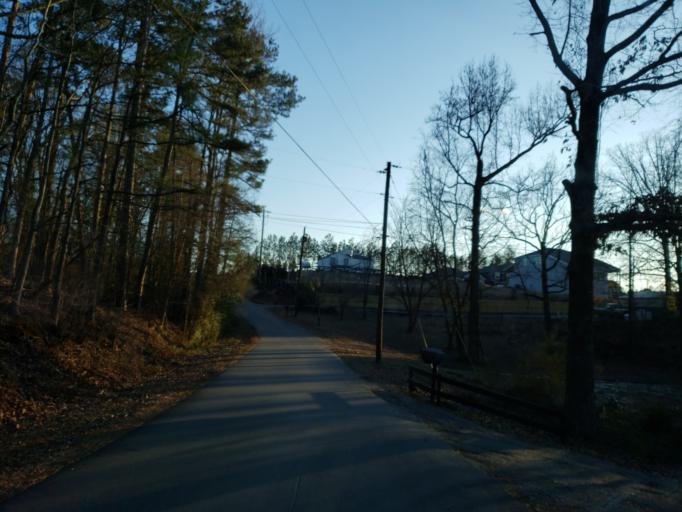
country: US
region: Georgia
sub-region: Cherokee County
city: Woodstock
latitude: 34.0949
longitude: -84.4845
